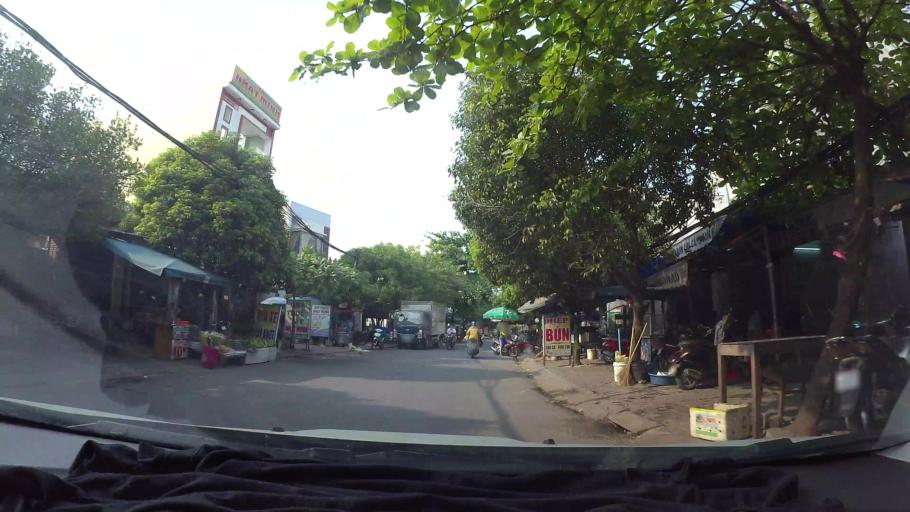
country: VN
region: Da Nang
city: Lien Chieu
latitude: 16.0541
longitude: 108.1693
